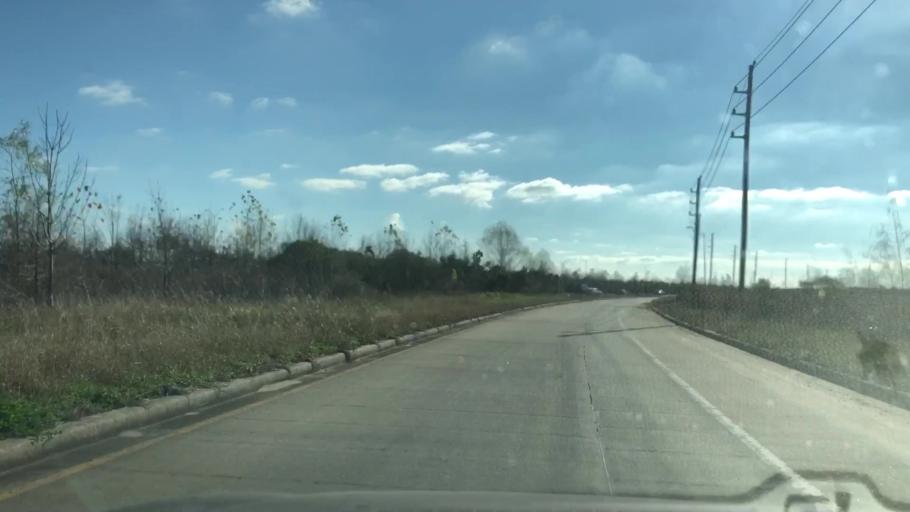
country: US
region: Texas
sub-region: Harris County
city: Cloverleaf
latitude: 29.8293
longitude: -95.1746
